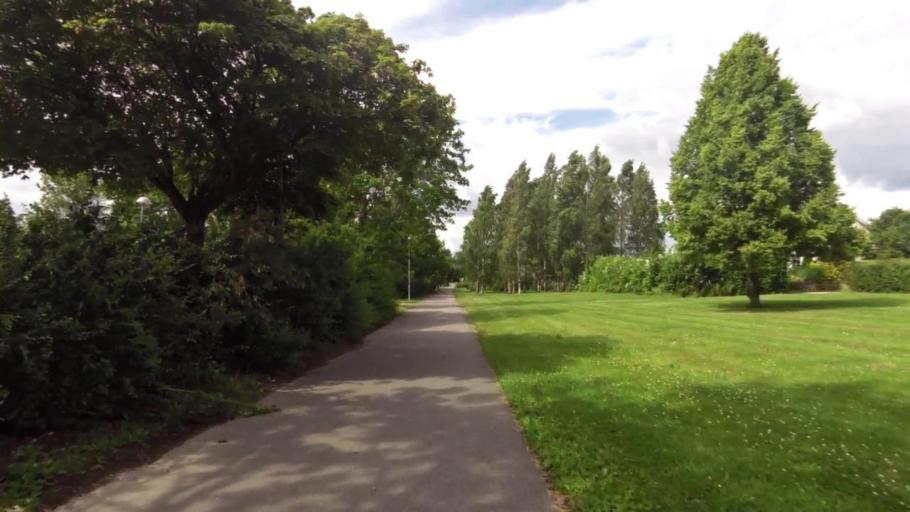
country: SE
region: OEstergoetland
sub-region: Linkopings Kommun
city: Malmslatt
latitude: 58.4159
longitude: 15.5634
